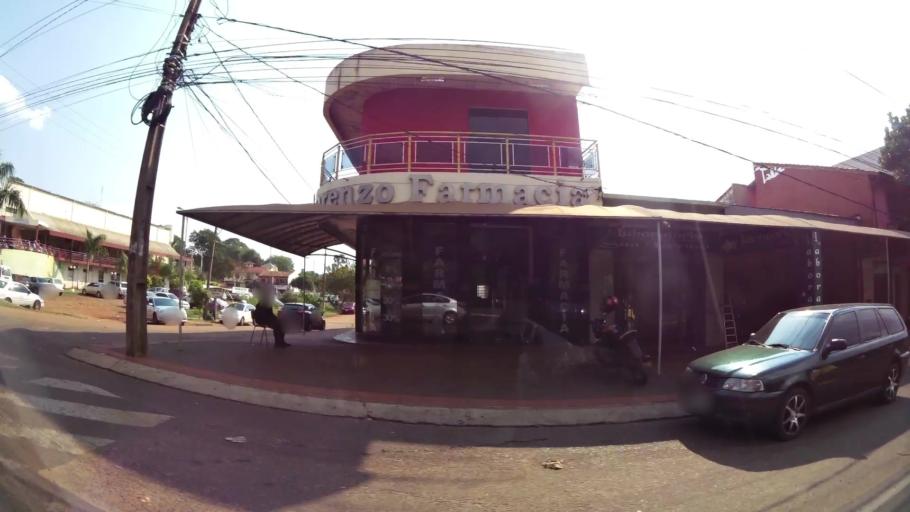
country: PY
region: Alto Parana
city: Presidente Franco
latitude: -25.5320
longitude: -54.6347
